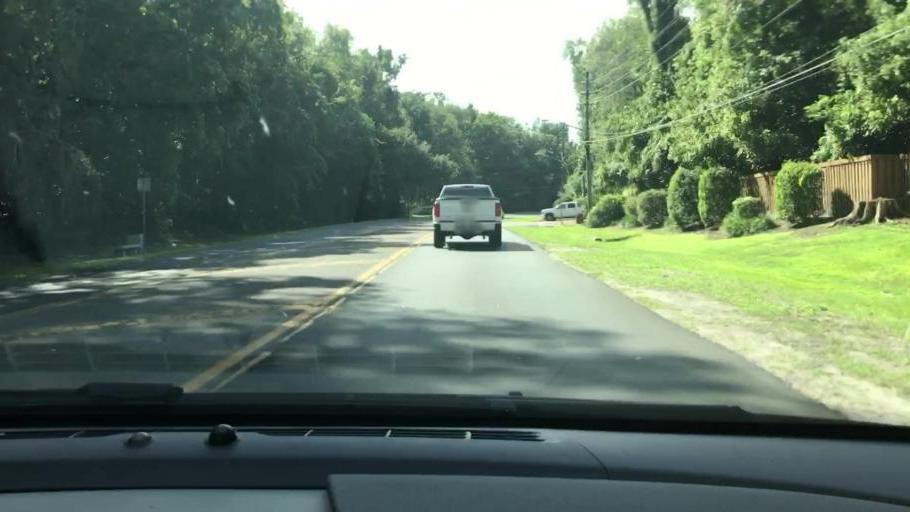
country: US
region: Florida
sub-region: Alachua County
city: Gainesville
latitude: 29.6450
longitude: -82.3995
